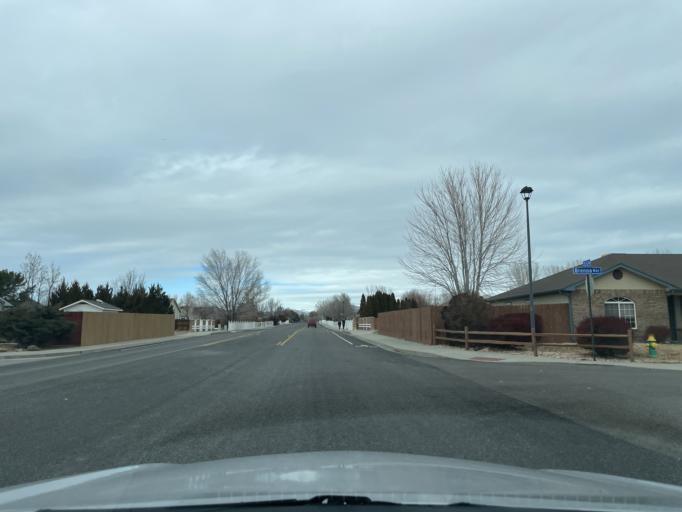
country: US
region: Colorado
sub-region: Mesa County
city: Grand Junction
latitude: 39.1002
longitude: -108.5801
